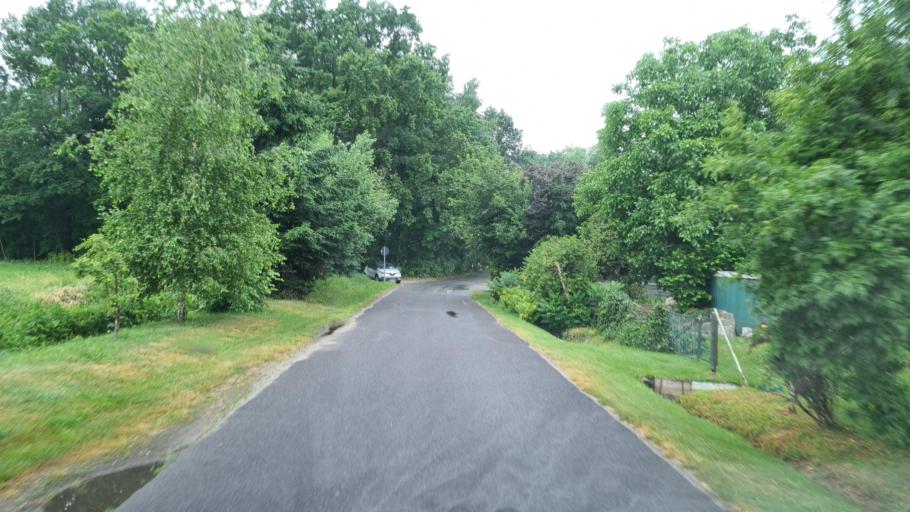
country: DE
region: Brandenburg
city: Lindenau
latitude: 51.3925
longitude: 13.7241
